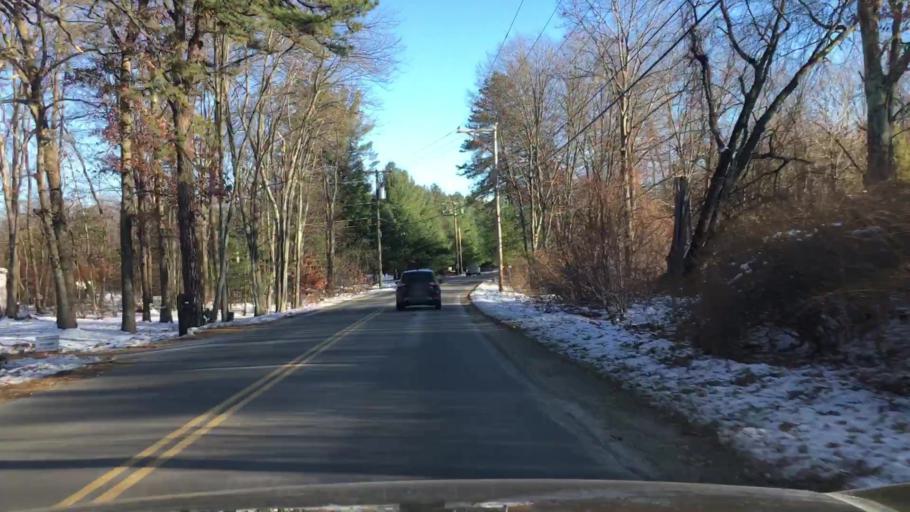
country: US
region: New Hampshire
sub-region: Hillsborough County
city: Hollis
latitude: 42.8163
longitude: -71.5722
